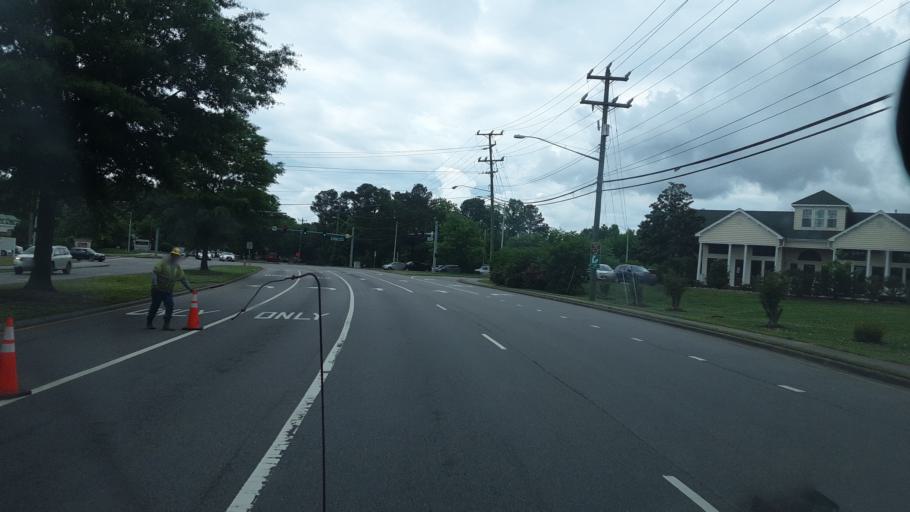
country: US
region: Virginia
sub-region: City of Virginia Beach
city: Virginia Beach
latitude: 36.7647
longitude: -76.0153
